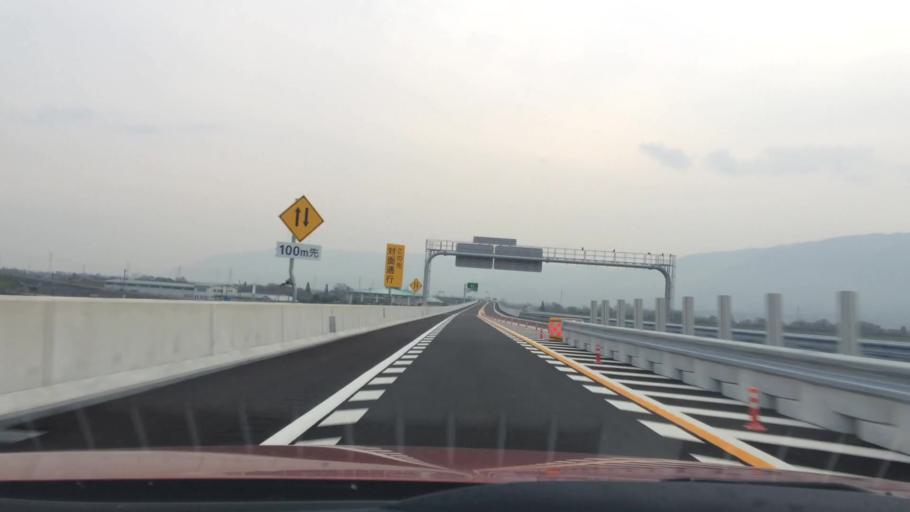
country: JP
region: Gifu
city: Ogaki
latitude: 35.3032
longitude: 136.5785
